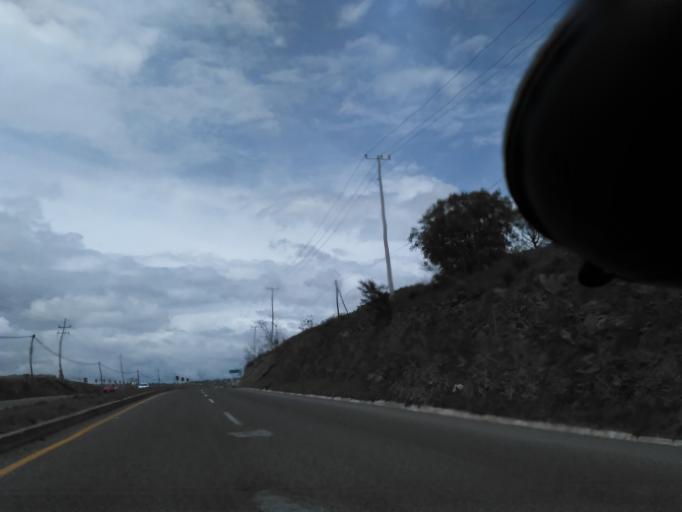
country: MX
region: Hidalgo
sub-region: Atotonilco de Tula
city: Paseos de la Pradera
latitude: 19.9054
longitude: -99.2408
